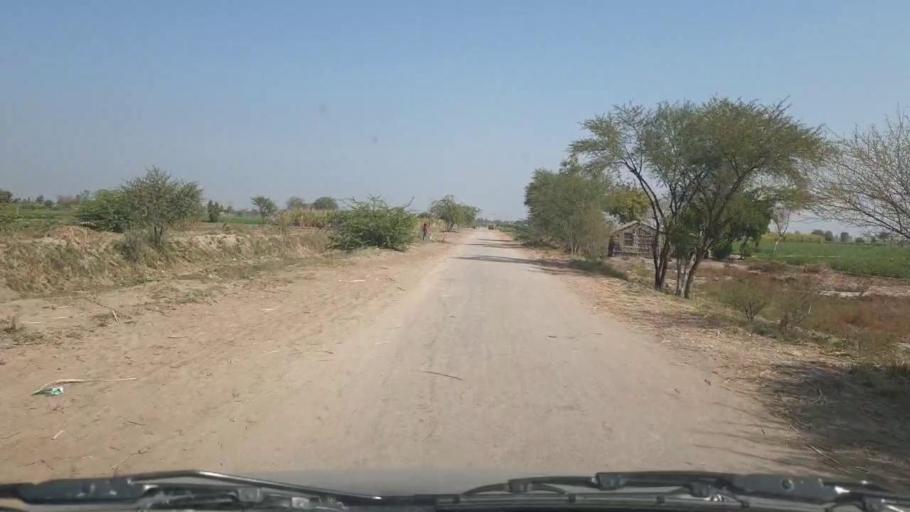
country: PK
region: Sindh
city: Samaro
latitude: 25.2914
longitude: 69.2891
